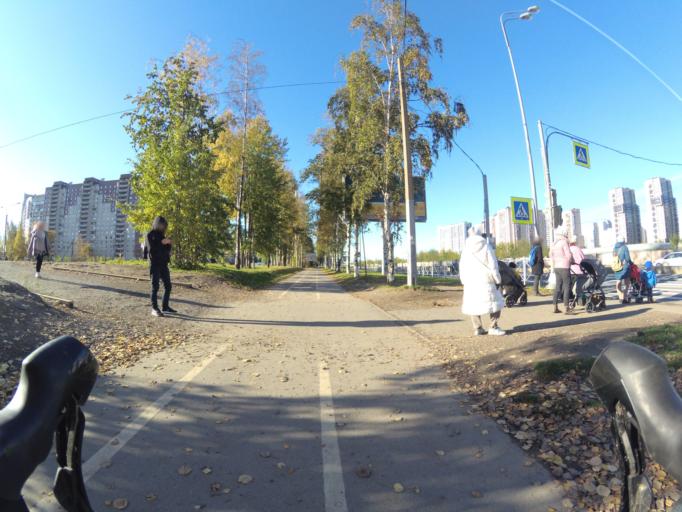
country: RU
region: Leningrad
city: Untolovo
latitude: 59.9934
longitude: 30.2048
